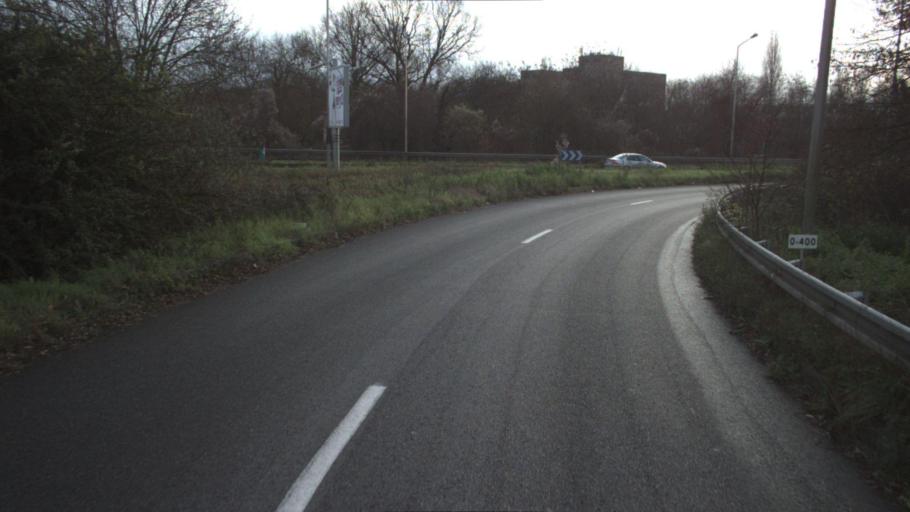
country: FR
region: Ile-de-France
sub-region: Departement de l'Essonne
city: Ris-Orangis
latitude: 48.6368
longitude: 2.4142
